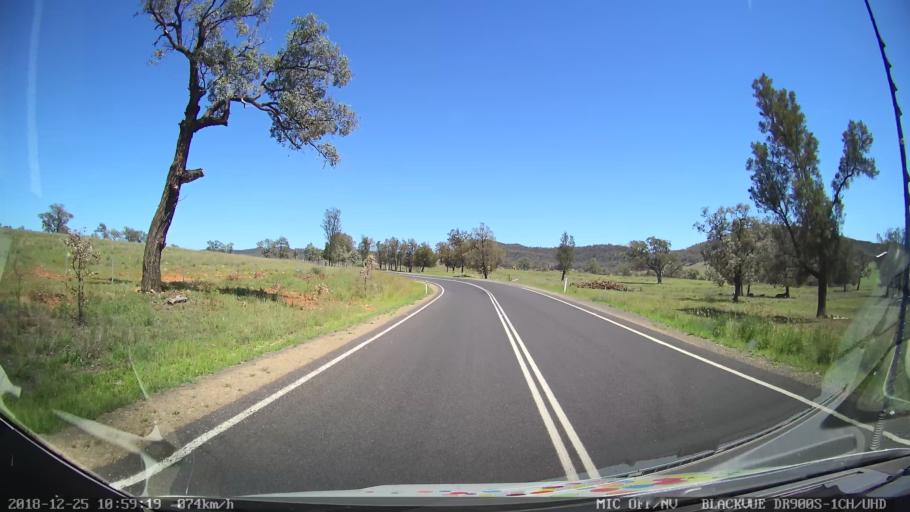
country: AU
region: New South Wales
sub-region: Upper Hunter Shire
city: Merriwa
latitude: -32.4030
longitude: 150.2297
